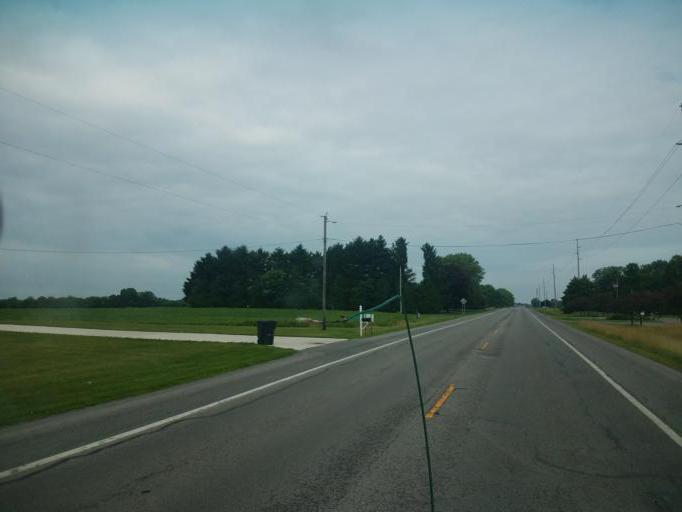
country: US
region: Ohio
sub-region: Hardin County
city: Kenton
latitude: 40.6576
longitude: -83.6382
